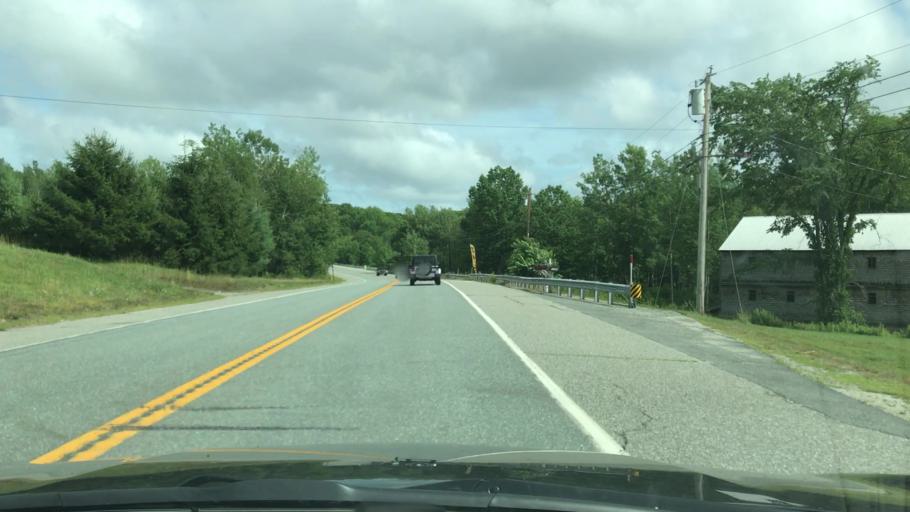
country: US
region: Maine
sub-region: Hancock County
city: Surry
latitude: 44.5624
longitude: -68.5871
